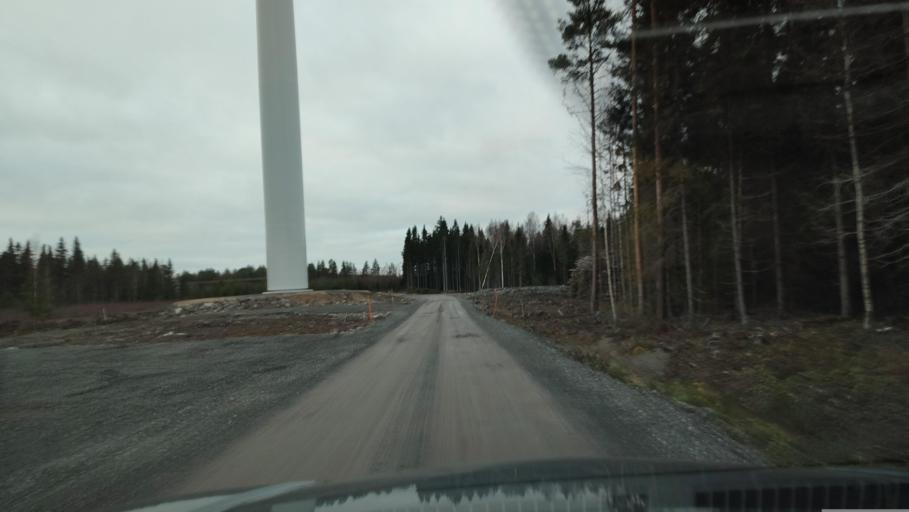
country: FI
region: Southern Ostrobothnia
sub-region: Suupohja
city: Karijoki
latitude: 62.2194
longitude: 21.5983
